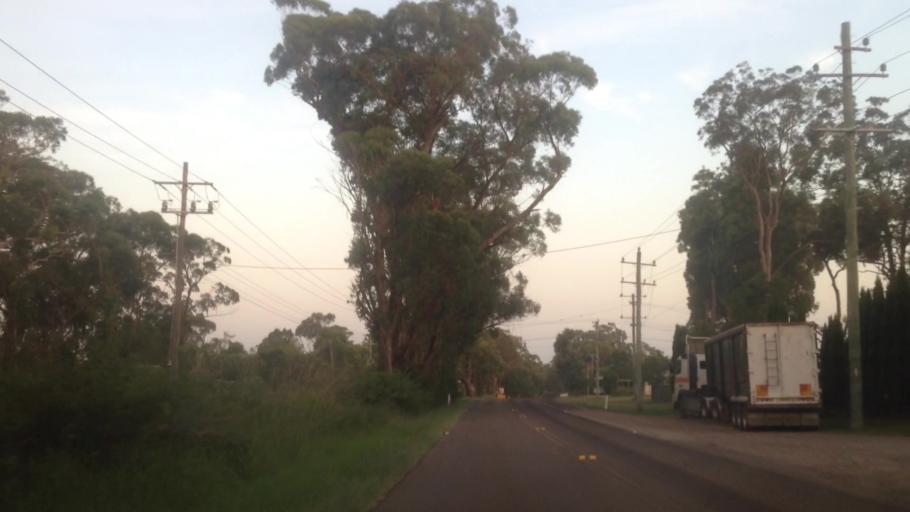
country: AU
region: New South Wales
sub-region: Lake Macquarie Shire
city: Dora Creek
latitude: -33.0759
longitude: 151.4871
